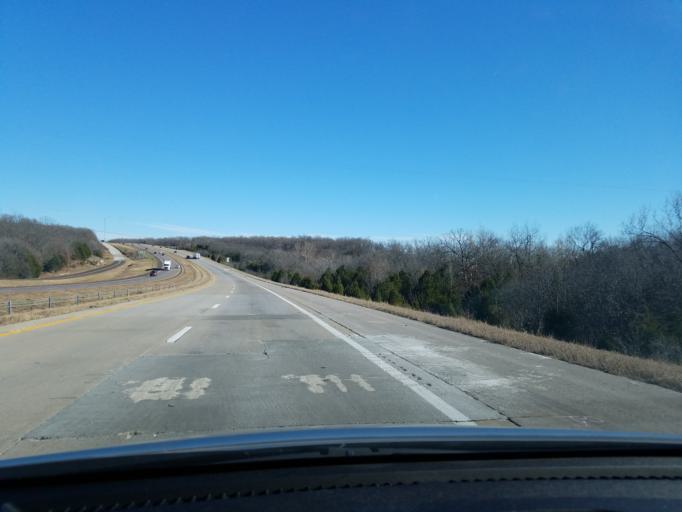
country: US
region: Missouri
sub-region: Pulaski County
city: Richland
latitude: 37.7532
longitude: -92.4966
